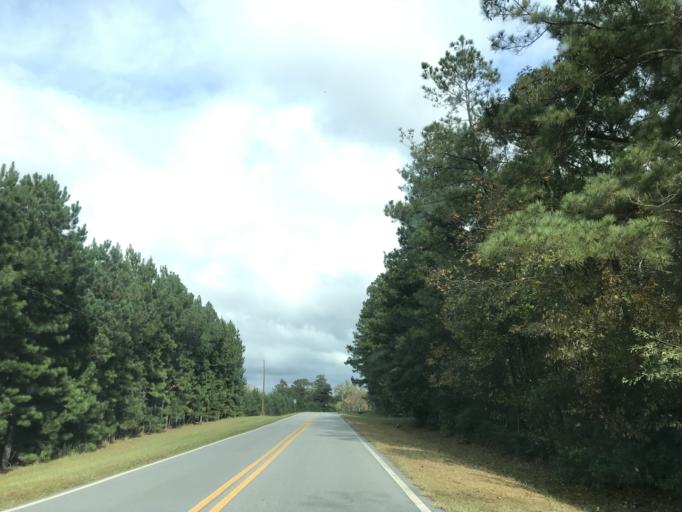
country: US
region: Georgia
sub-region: Jones County
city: Gray
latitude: 32.9672
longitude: -83.4908
